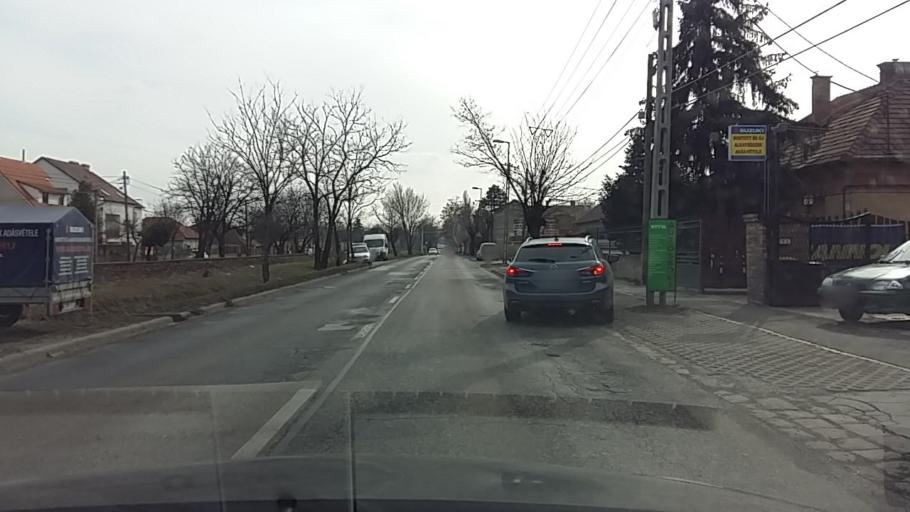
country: HU
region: Budapest
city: Budapest XVIII. keruelet
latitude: 47.4119
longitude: 19.1754
